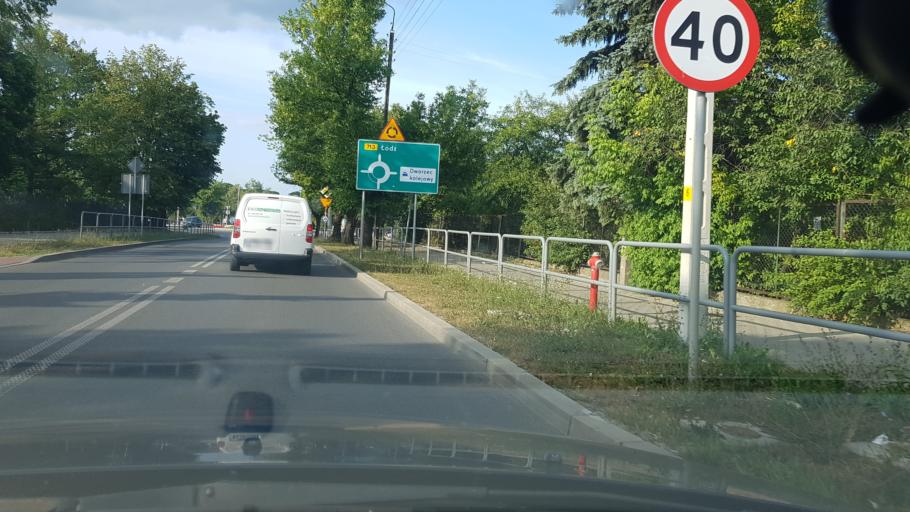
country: PL
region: Lodz Voivodeship
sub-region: Powiat tomaszowski
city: Tomaszow Mazowiecki
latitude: 51.5456
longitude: 20.0139
